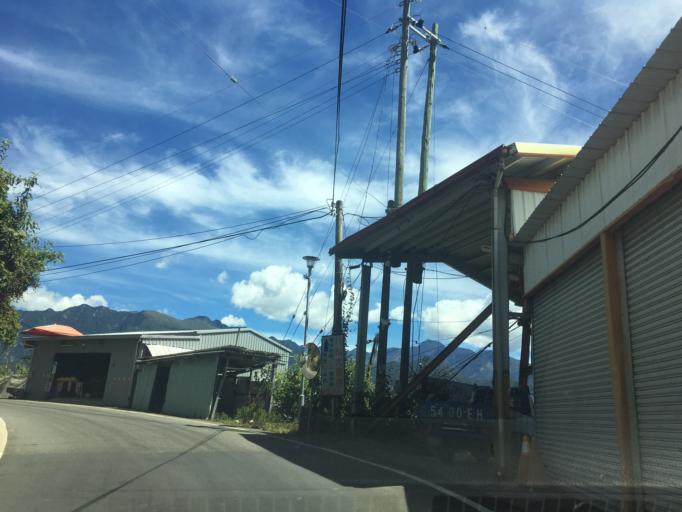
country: TW
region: Taiwan
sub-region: Nantou
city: Puli
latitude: 24.2576
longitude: 121.2637
